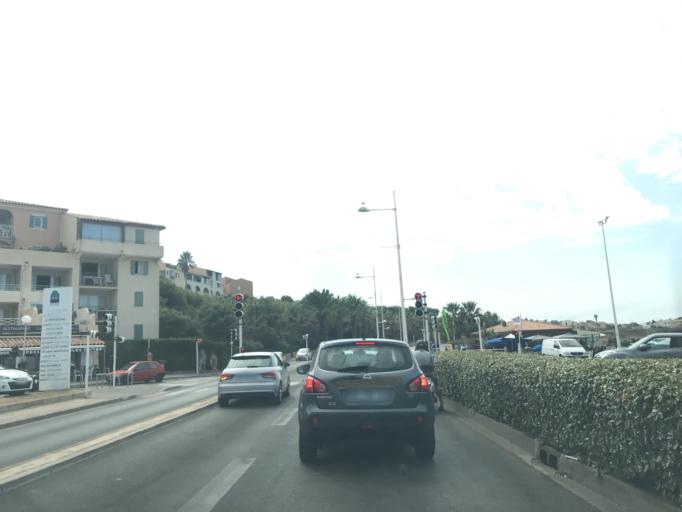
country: FR
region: Provence-Alpes-Cote d'Azur
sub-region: Departement du Var
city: Sanary-sur-Mer
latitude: 43.0964
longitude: 5.8126
